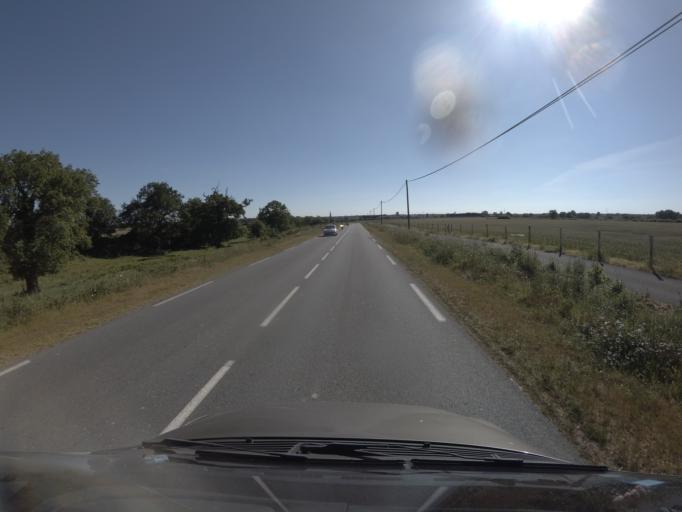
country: FR
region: Pays de la Loire
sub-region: Departement de Maine-et-Loire
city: Torfou
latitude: 47.0267
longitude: -1.1012
